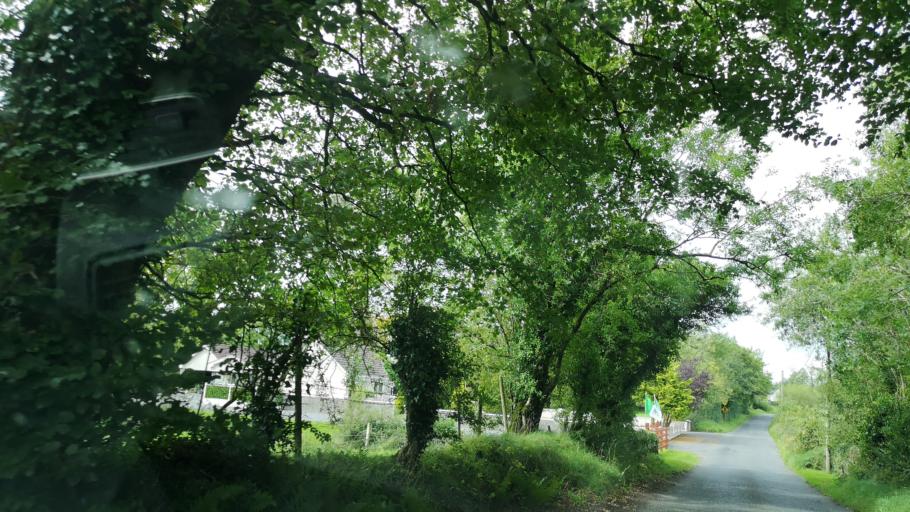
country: IE
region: Connaught
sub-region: County Galway
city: Loughrea
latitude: 53.3018
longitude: -8.6023
